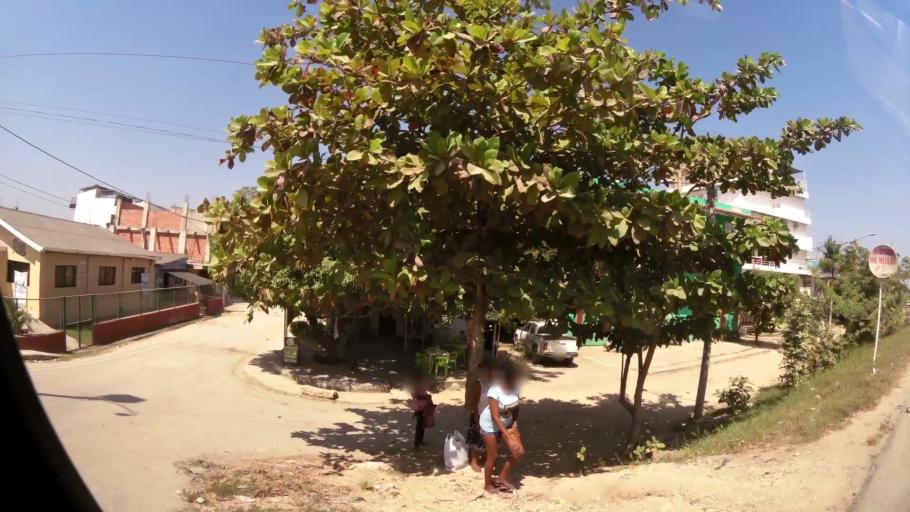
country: CO
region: Bolivar
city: Cartagena
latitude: 10.3830
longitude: -75.4505
